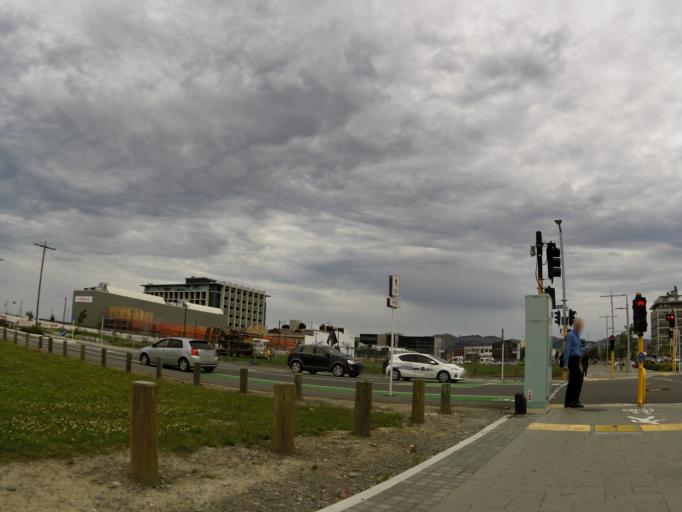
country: NZ
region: Canterbury
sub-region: Christchurch City
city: Christchurch
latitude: -43.5320
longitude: 172.6399
